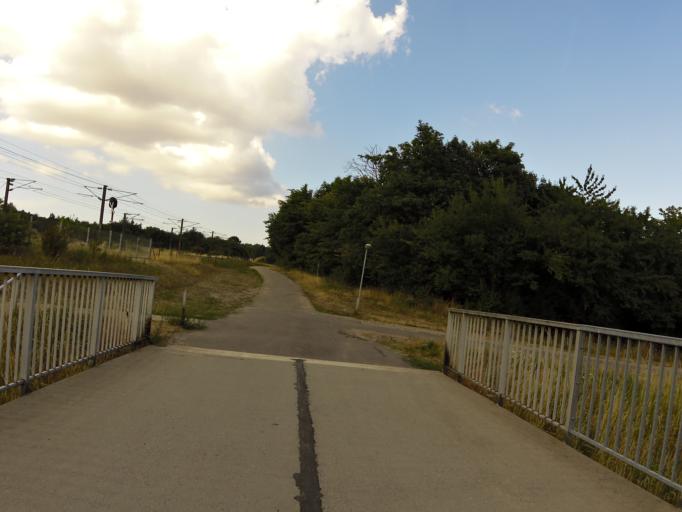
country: DK
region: Capital Region
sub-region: Fredensborg Kommune
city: Niva
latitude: 55.9353
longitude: 12.5084
